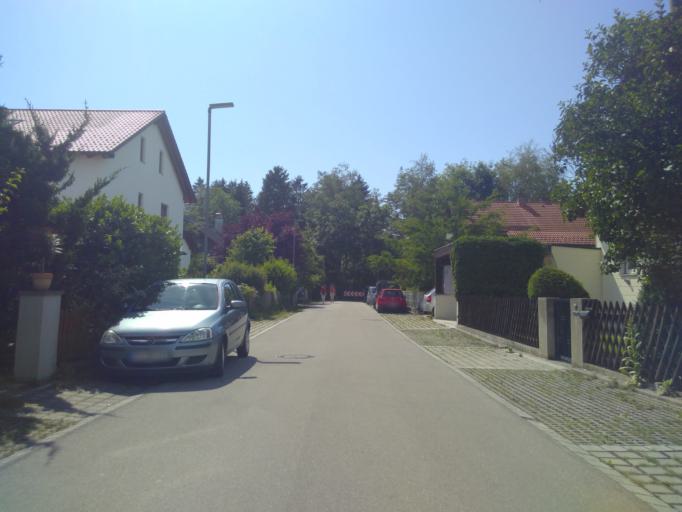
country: DE
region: Bavaria
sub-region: Upper Bavaria
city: Grobenzell
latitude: 48.1977
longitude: 11.3642
